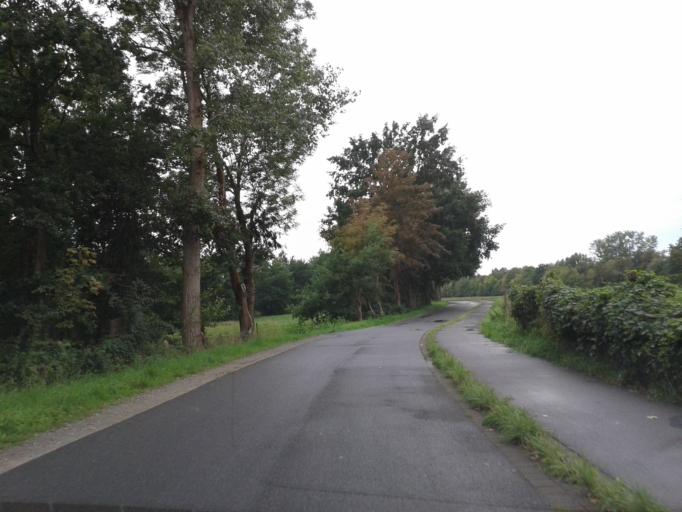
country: DE
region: Lower Saxony
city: Luechow
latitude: 52.9467
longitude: 11.1506
